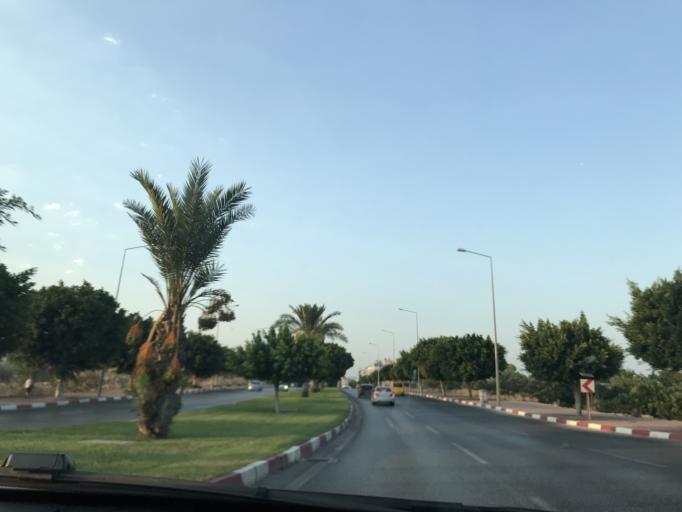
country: TR
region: Antalya
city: Antalya
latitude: 36.8693
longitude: 30.6402
